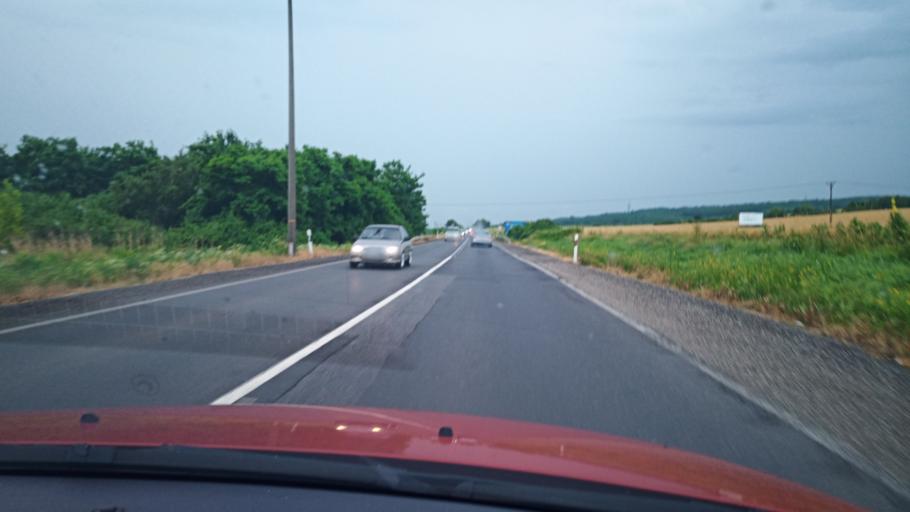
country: HU
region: Borsod-Abauj-Zemplen
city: Malyi
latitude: 48.0485
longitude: 20.8006
